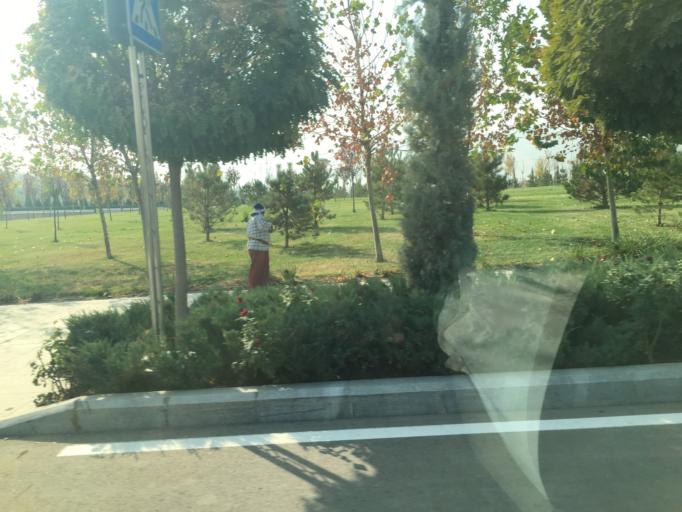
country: TM
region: Ahal
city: Ashgabat
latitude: 37.9365
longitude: 58.3207
